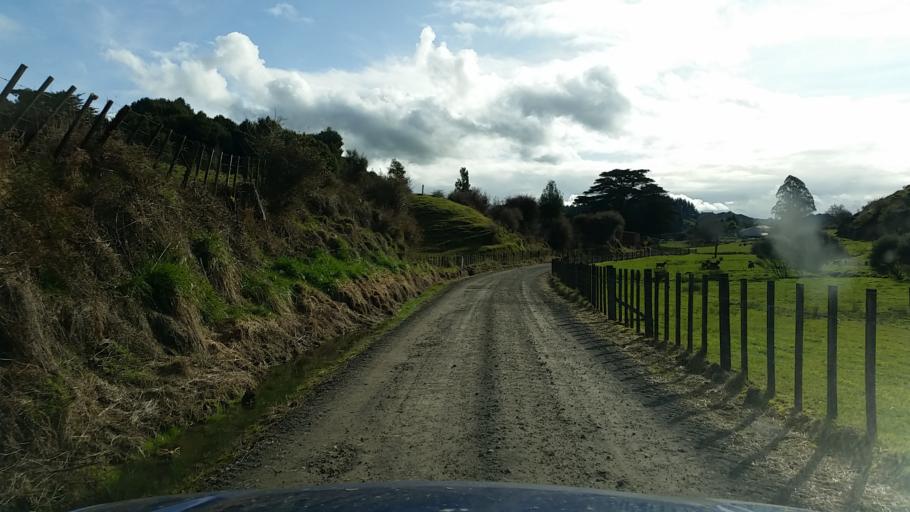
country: NZ
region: Taranaki
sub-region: South Taranaki District
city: Eltham
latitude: -39.2606
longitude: 174.5784
